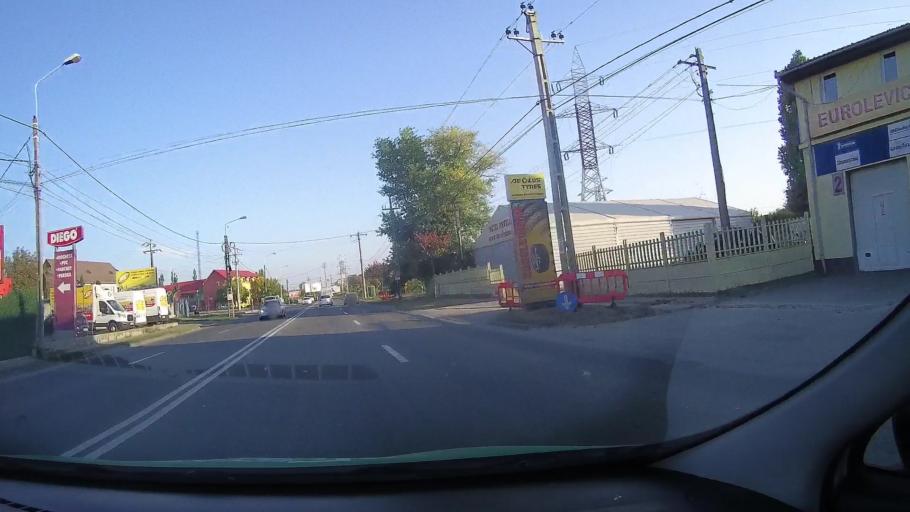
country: RO
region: Bihor
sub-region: Comuna Biharea
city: Oradea
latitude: 47.0869
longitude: 21.9129
